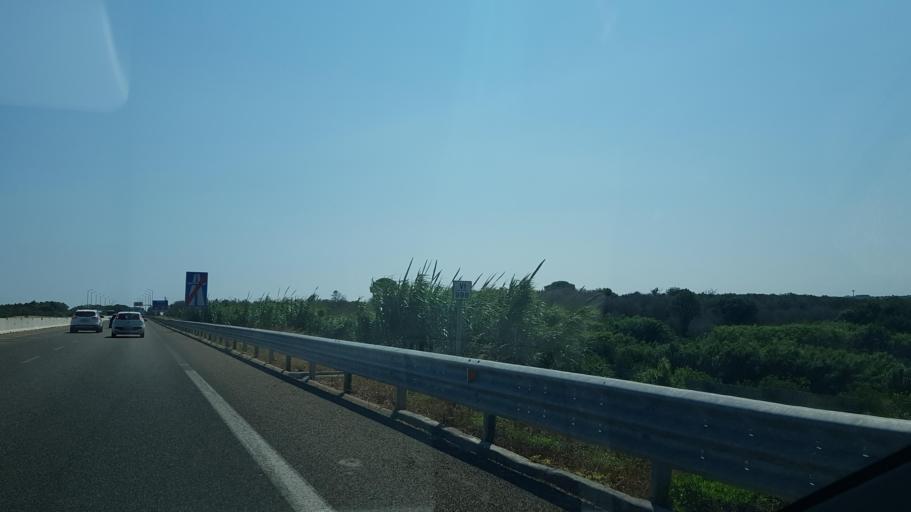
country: IT
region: Apulia
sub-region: Provincia di Lecce
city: Otranto
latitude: 40.1450
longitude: 18.4668
